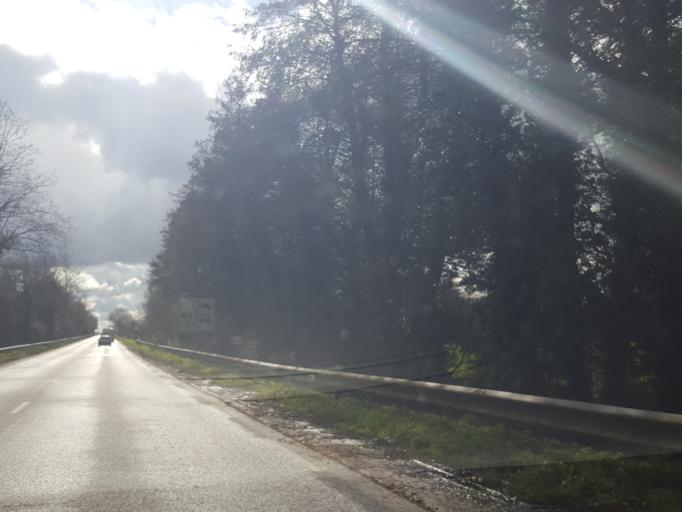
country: FR
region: Pays de la Loire
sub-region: Departement de la Vendee
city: Belleville-sur-Vie
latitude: 46.7636
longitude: -1.4310
